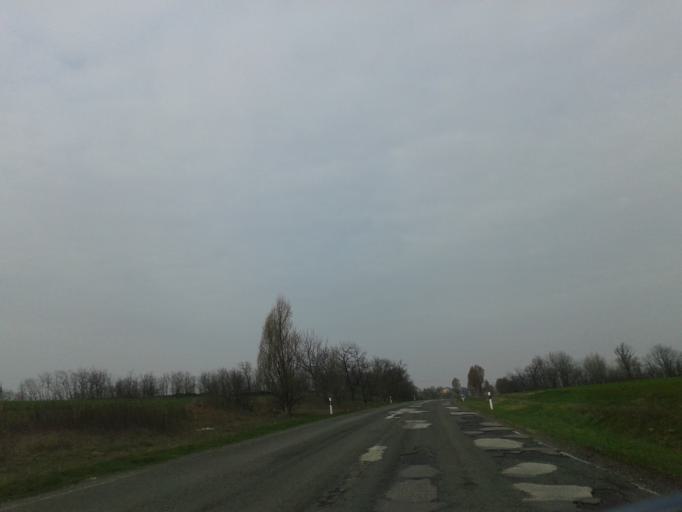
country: HU
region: Komarom-Esztergom
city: Acs
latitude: 47.7222
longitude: 18.0226
